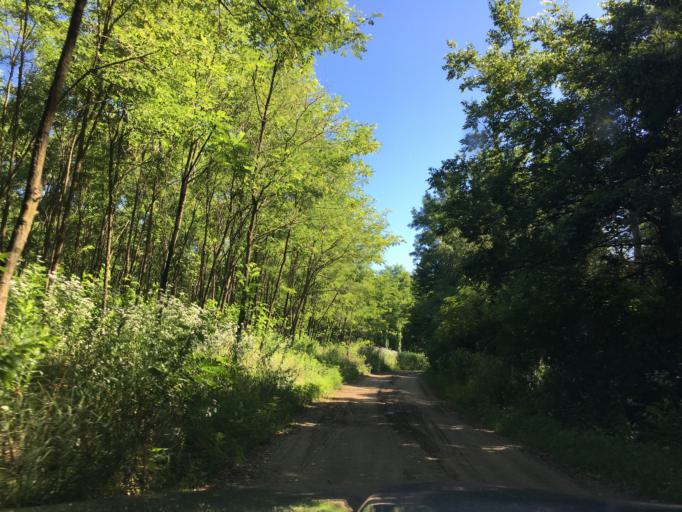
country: HU
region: Hajdu-Bihar
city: Hajdusamson
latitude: 47.5337
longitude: 21.7851
